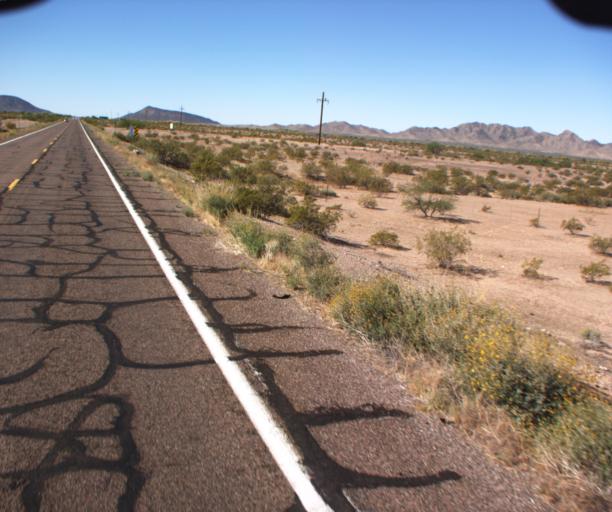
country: US
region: Arizona
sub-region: Maricopa County
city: Gila Bend
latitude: 32.8201
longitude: -112.7884
